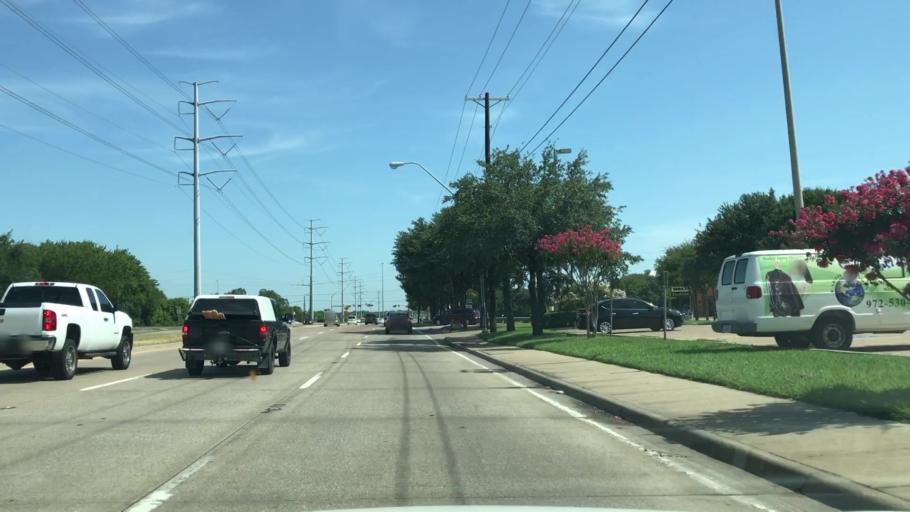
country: US
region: Texas
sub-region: Dallas County
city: Garland
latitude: 32.9448
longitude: -96.6212
